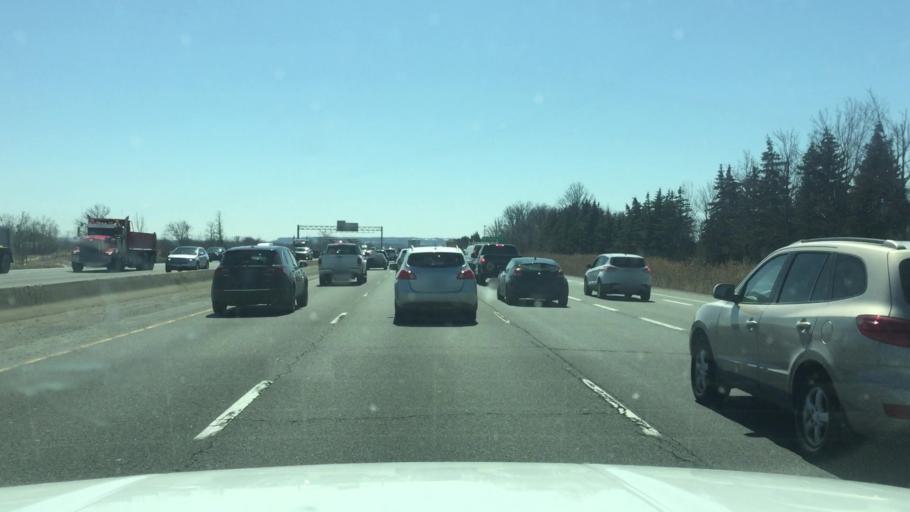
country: CA
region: Ontario
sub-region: Halton
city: Milton
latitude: 43.5829
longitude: -79.8166
